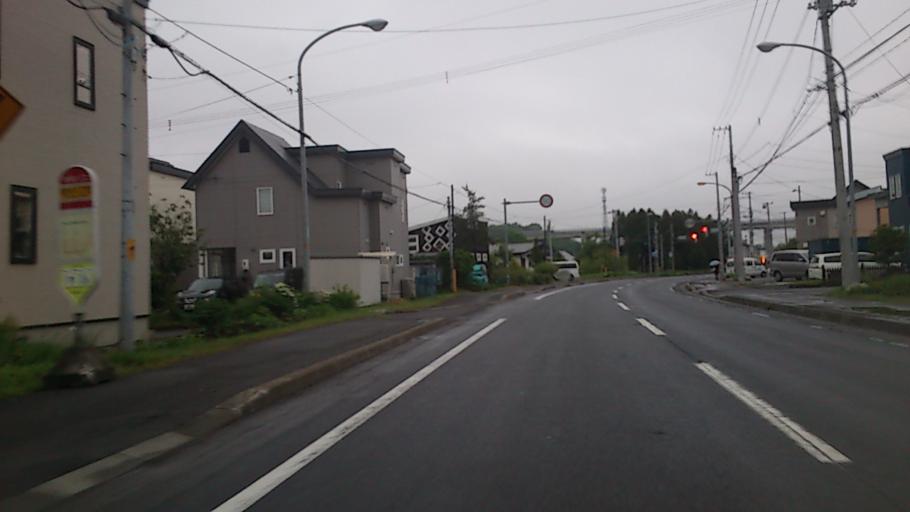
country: JP
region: Hokkaido
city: Chitose
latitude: 42.8184
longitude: 141.6253
